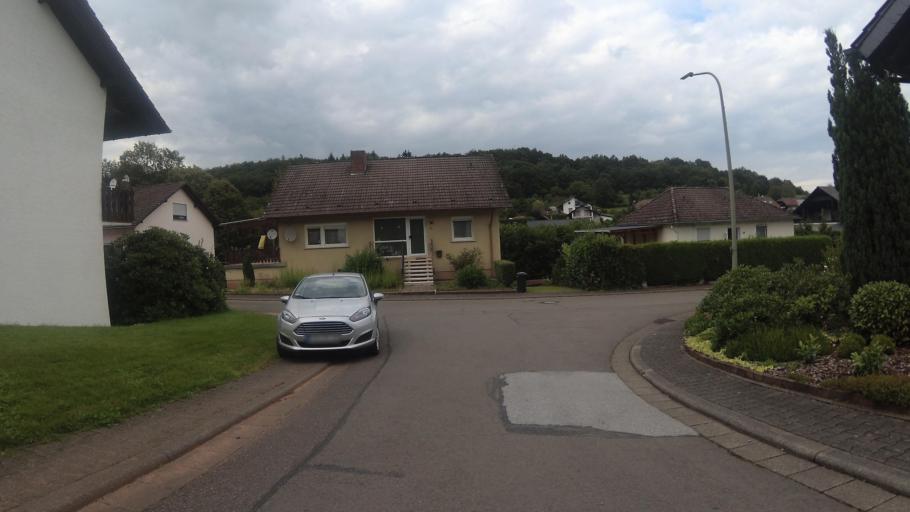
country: DE
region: Rheinland-Pfalz
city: Krottelbach
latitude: 49.4653
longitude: 7.3223
